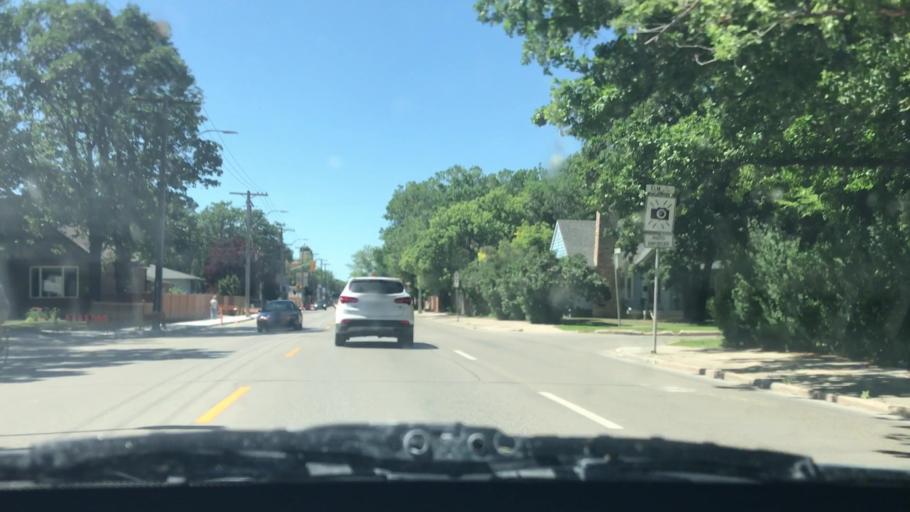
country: CA
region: Manitoba
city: Winnipeg
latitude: 49.8737
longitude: -97.1793
